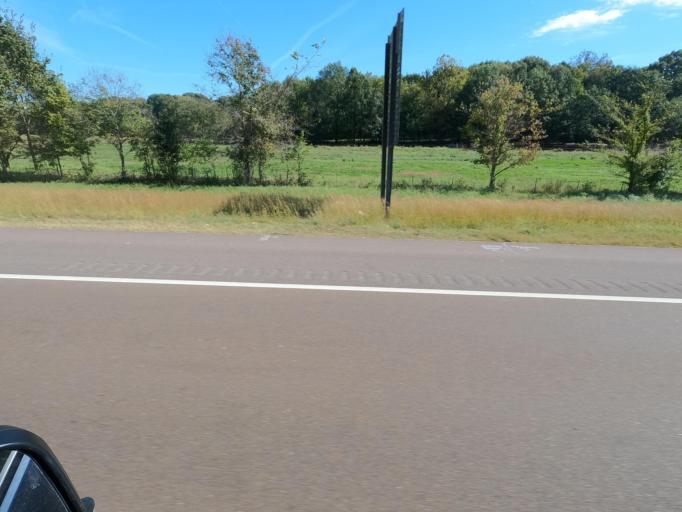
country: US
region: Tennessee
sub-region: Dyer County
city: Dyersburg
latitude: 36.0145
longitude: -89.3408
